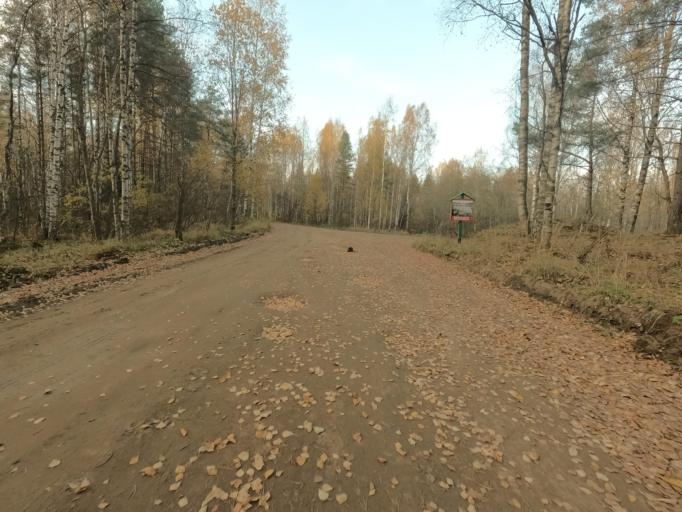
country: RU
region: Leningrad
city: Priladozhskiy
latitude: 59.7430
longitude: 31.3127
